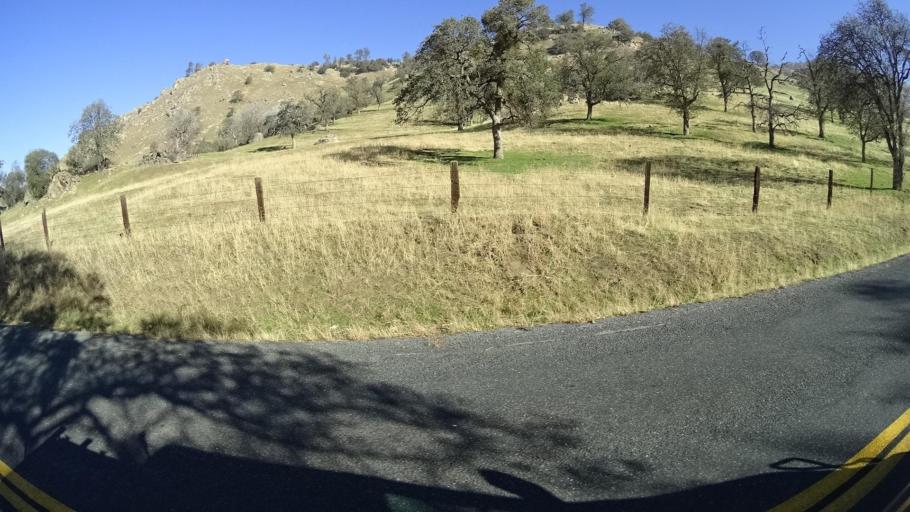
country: US
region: California
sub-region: Kern County
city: Alta Sierra
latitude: 35.7903
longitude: -118.8040
